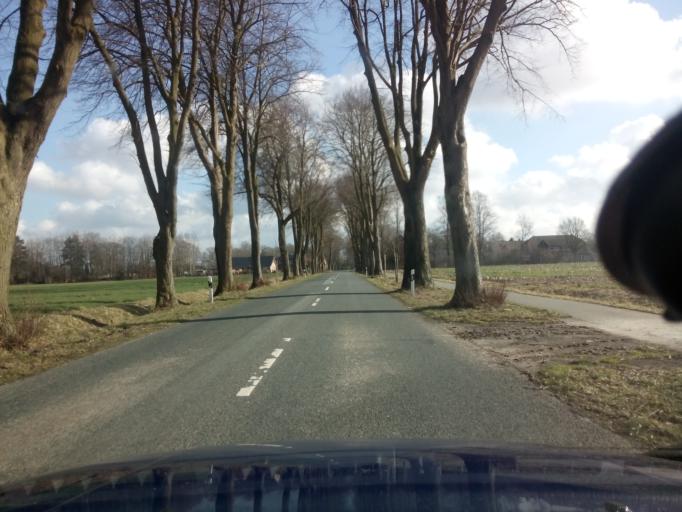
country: DE
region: Lower Saxony
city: Basdahl
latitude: 53.4152
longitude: 8.9856
